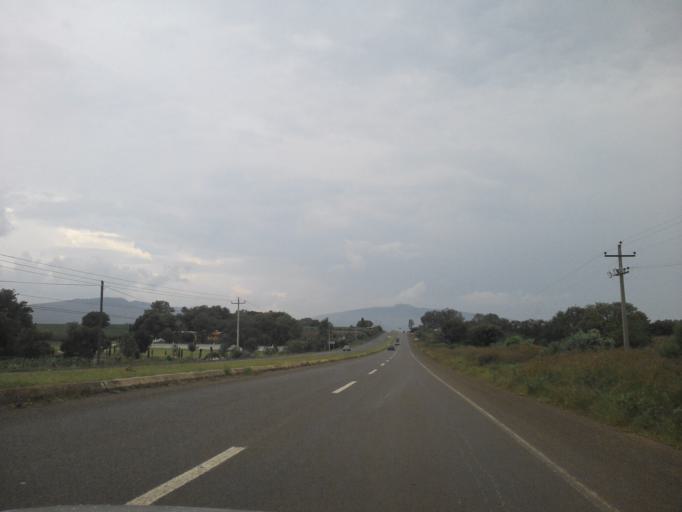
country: MX
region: Jalisco
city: San Jose de Gracia
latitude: 20.7331
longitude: -102.4941
